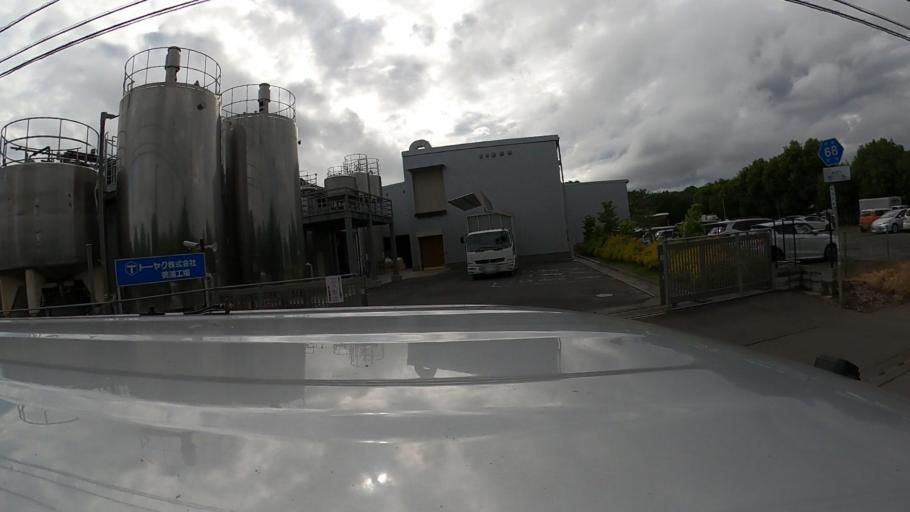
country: JP
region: Ibaraki
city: Inashiki
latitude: 36.0046
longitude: 140.2844
